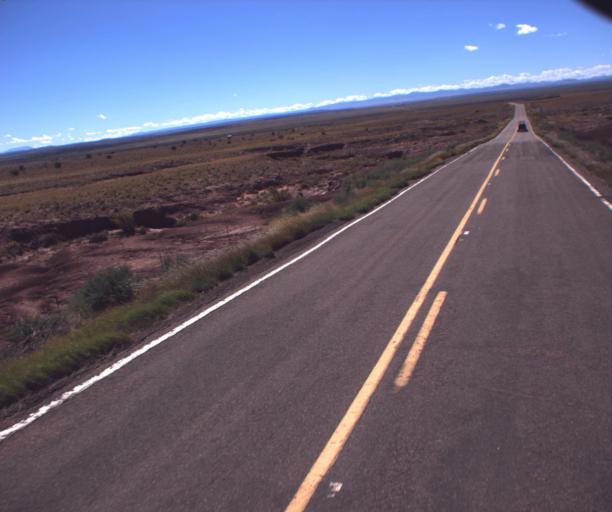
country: US
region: Arizona
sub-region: Apache County
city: Saint Johns
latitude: 34.6454
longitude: -109.3028
